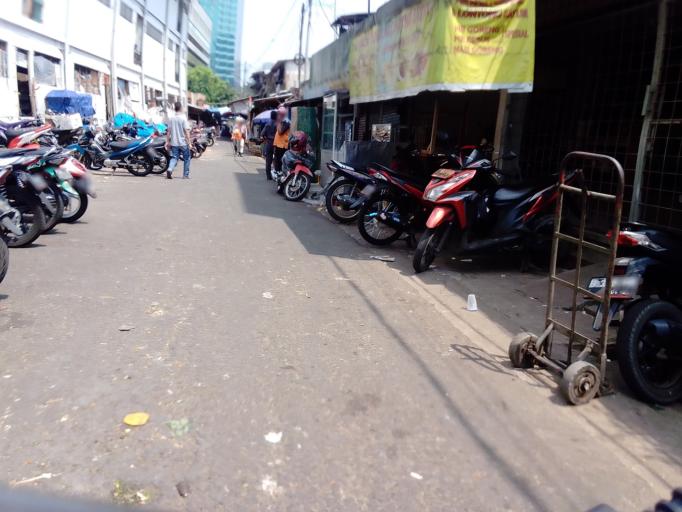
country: ID
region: Jakarta Raya
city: Jakarta
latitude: -6.2152
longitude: 106.8149
